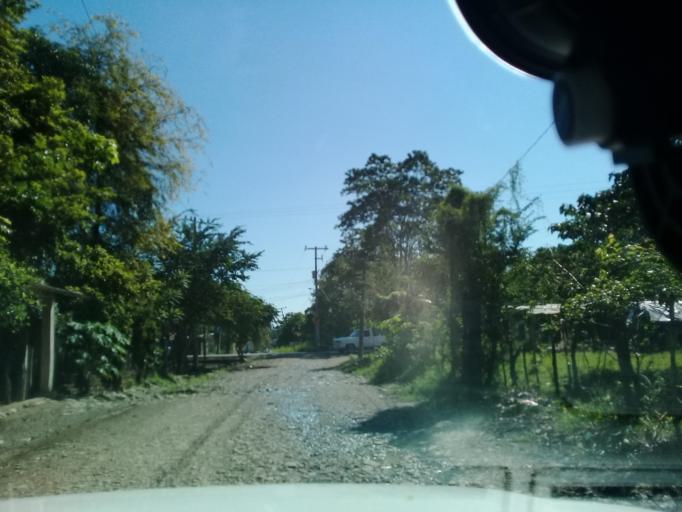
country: MX
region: Hidalgo
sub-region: Huejutla de Reyes
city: Parque de Poblamiento Solidaridad
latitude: 21.1605
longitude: -98.4074
